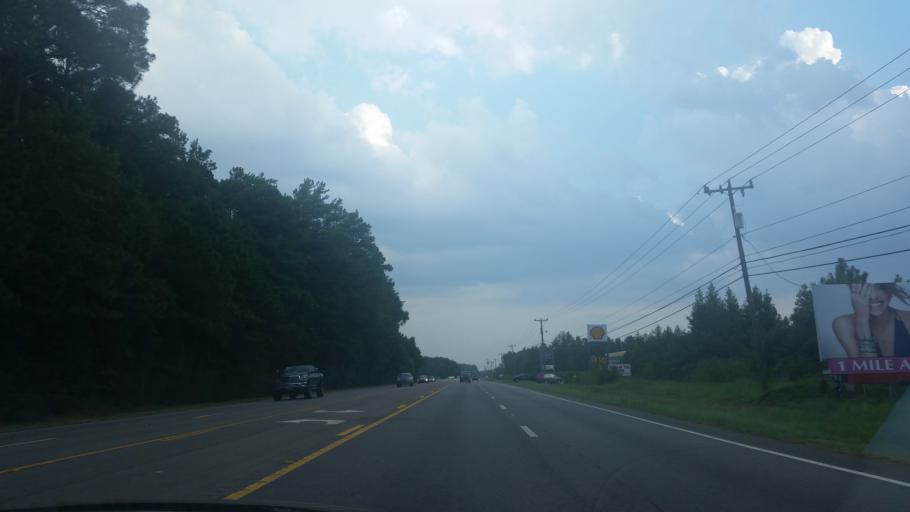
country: US
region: North Carolina
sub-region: Dare County
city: Southern Shores
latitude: 36.2251
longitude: -75.8714
